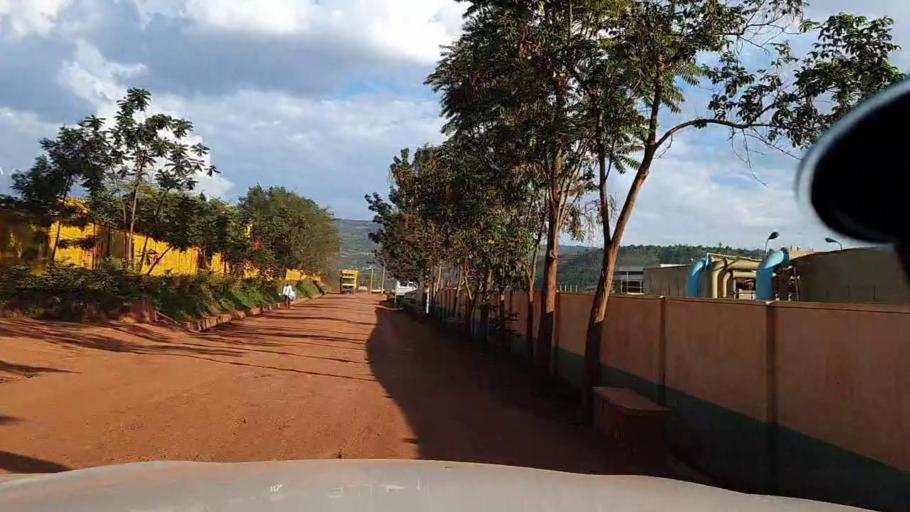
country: RW
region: Kigali
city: Kigali
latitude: -1.9419
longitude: 30.0016
